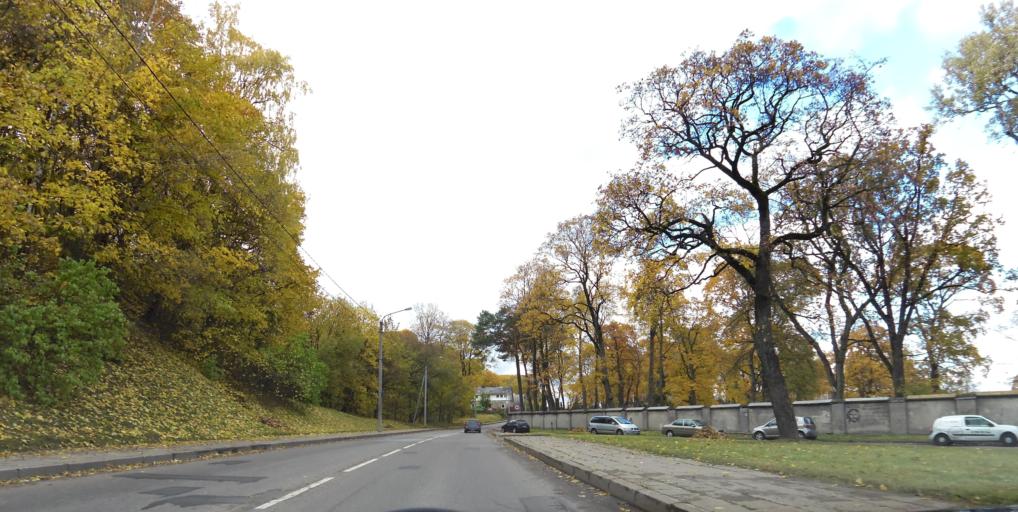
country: LT
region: Vilnius County
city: Rasos
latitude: 54.6670
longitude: 25.3045
